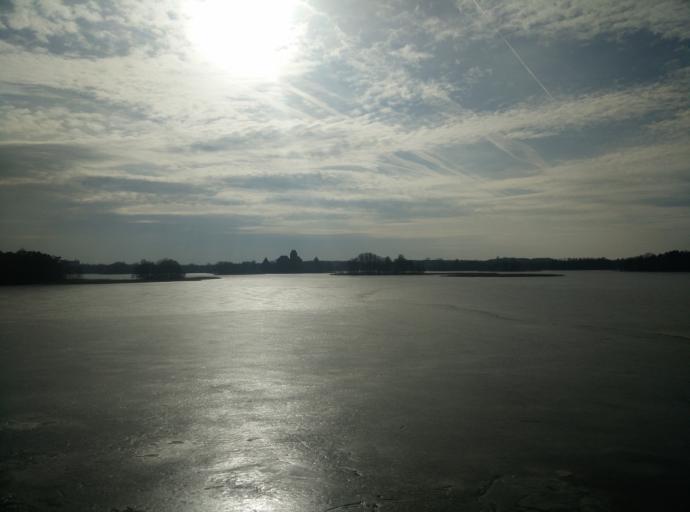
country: LT
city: Trakai
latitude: 54.6596
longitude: 24.9432
